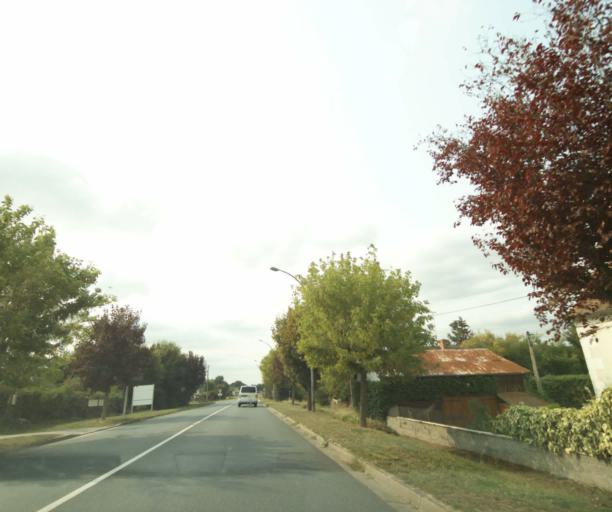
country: FR
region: Centre
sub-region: Departement de l'Indre
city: Chatillon-sur-Indre
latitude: 46.9965
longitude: 1.1574
